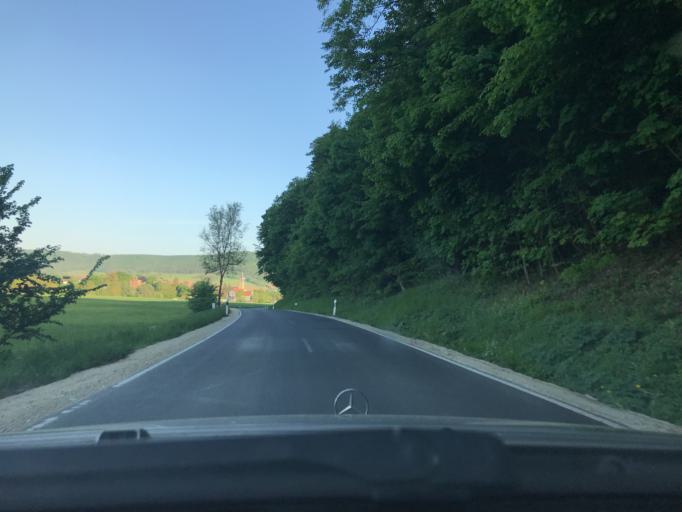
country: DE
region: Hesse
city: Wanfried
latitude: 51.1881
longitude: 10.1556
